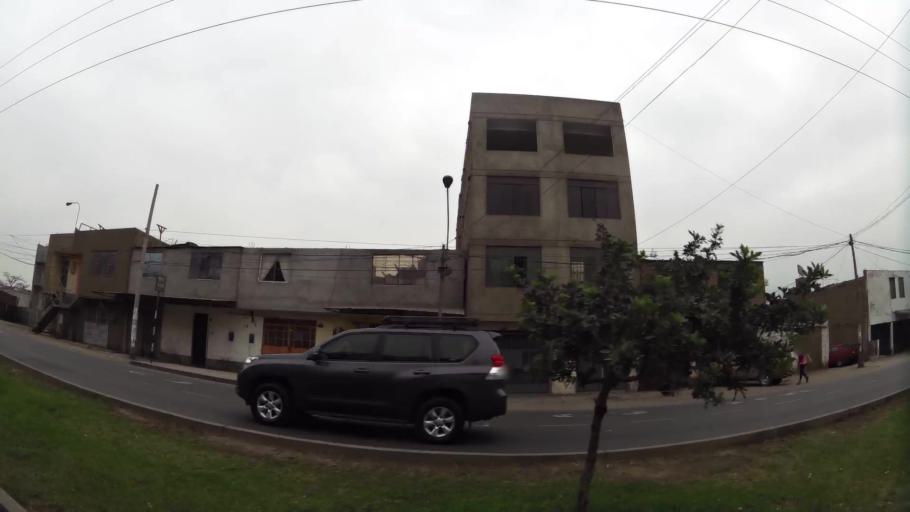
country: PE
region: Lima
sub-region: Lima
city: Independencia
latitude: -11.9753
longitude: -76.9921
